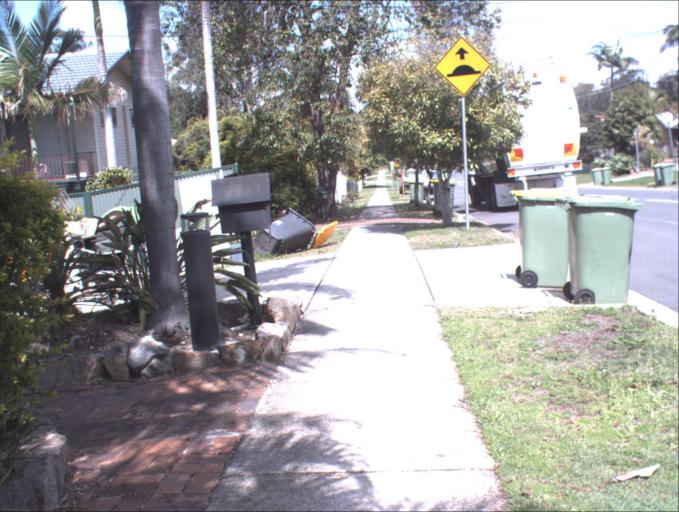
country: AU
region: Queensland
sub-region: Logan
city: Park Ridge South
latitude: -27.6661
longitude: 153.0288
